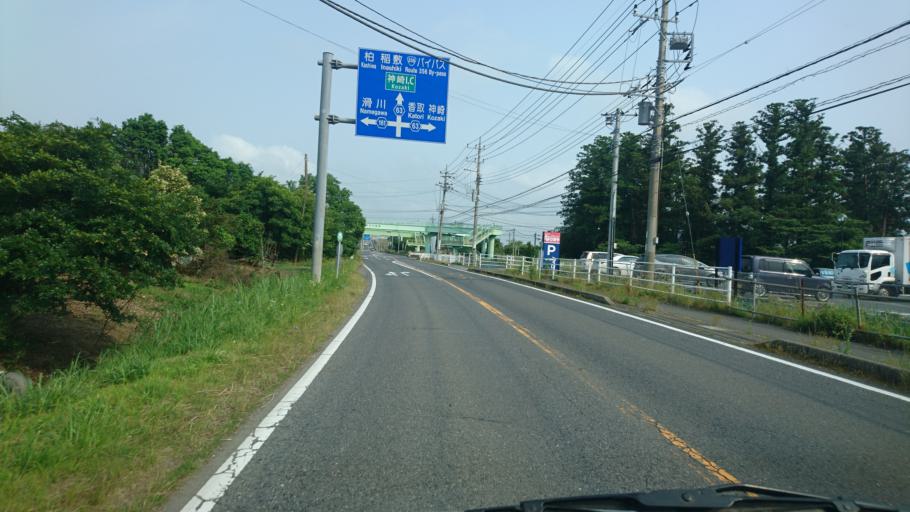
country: JP
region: Ibaraki
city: Edosaki
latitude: 35.8770
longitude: 140.3544
